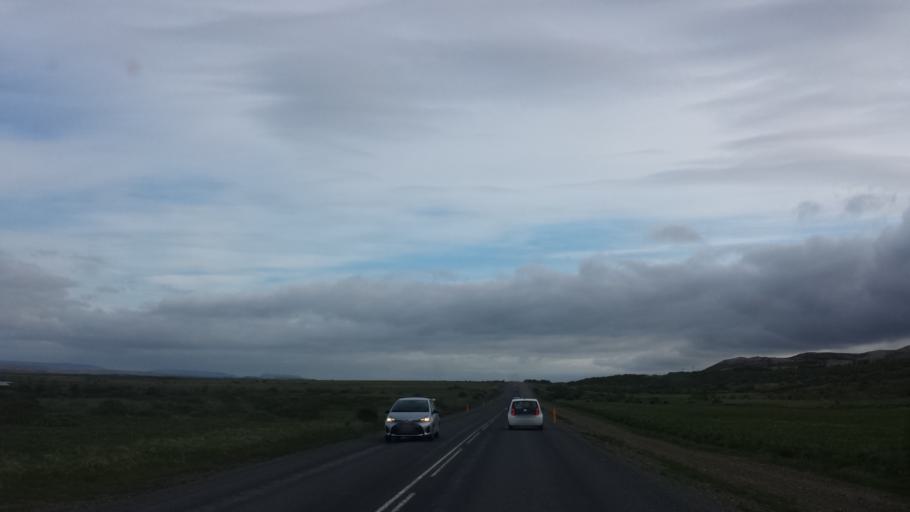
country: IS
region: South
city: Selfoss
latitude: 64.2952
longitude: -20.3346
